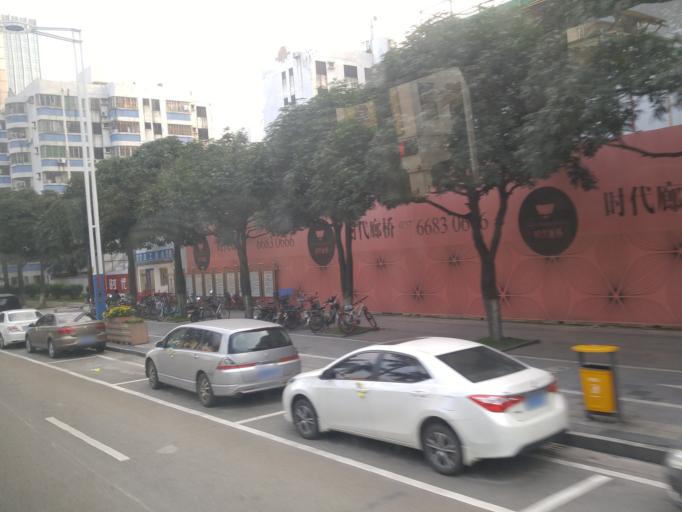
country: CN
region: Guangdong
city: Foshan
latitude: 23.0634
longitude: 113.1403
